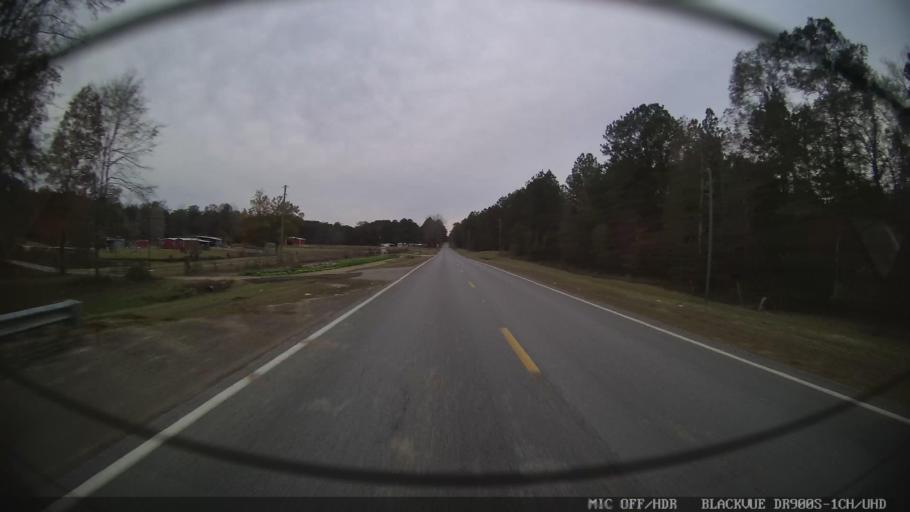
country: US
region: Mississippi
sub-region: Clarke County
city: Quitman
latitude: 32.0289
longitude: -88.8054
